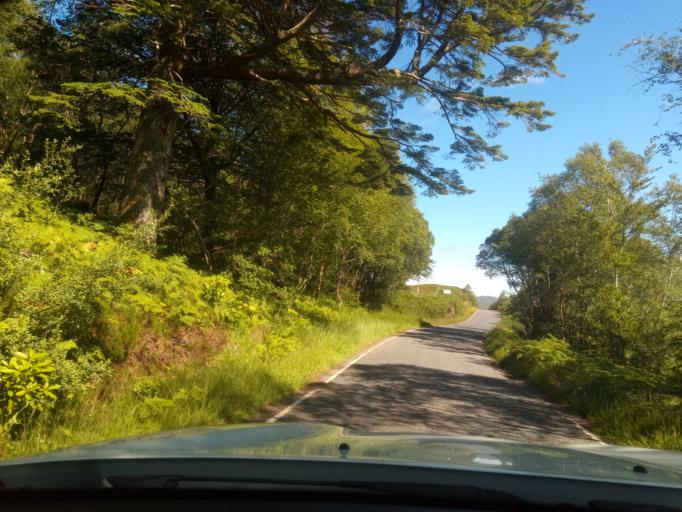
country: GB
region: Scotland
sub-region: Argyll and Bute
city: Isle Of Mull
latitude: 56.7334
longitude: -5.7772
